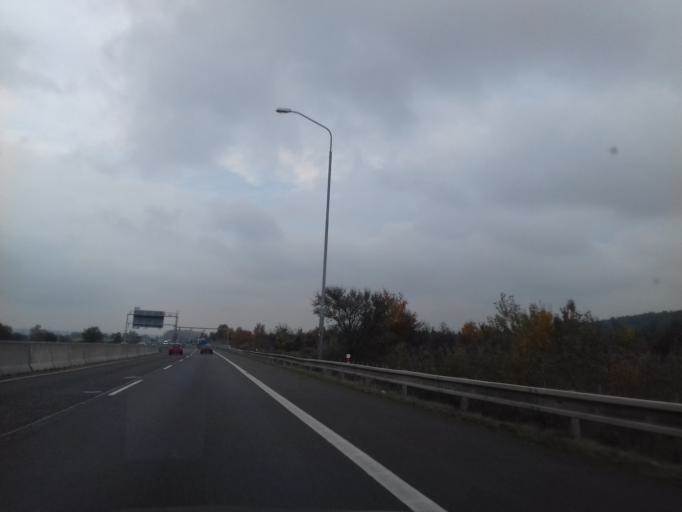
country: SK
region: Bratislavsky
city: Stupava
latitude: 48.2103
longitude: 17.0372
